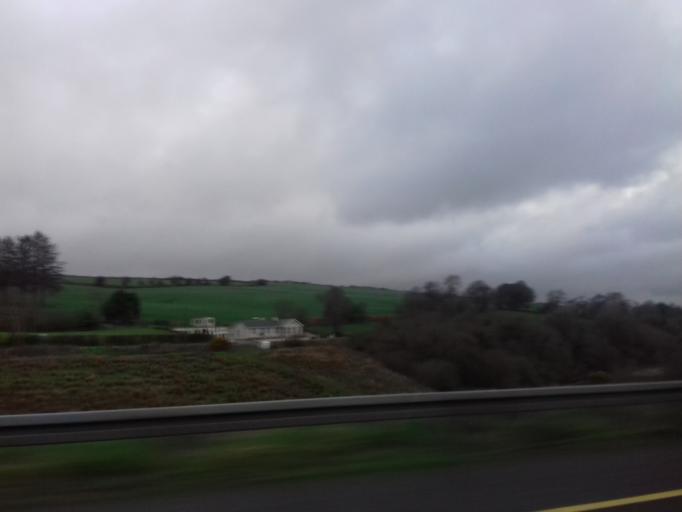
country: IE
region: Munster
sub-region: County Limerick
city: Abbeyfeale
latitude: 52.3127
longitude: -9.3628
